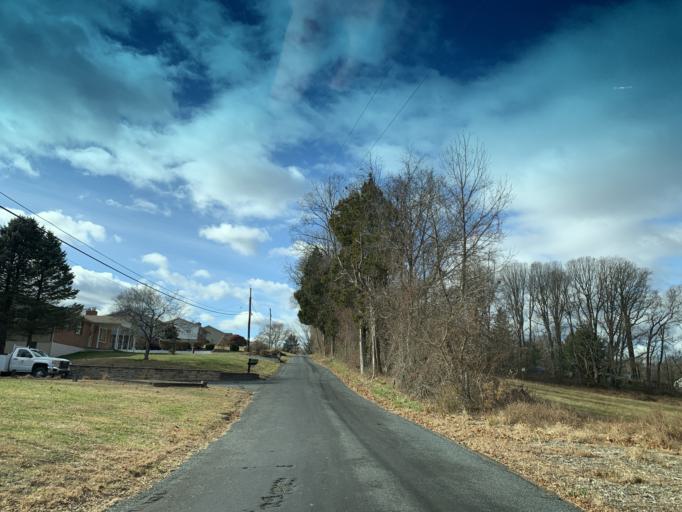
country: US
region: Maryland
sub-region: Harford County
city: Bel Air North
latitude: 39.5951
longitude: -76.4174
